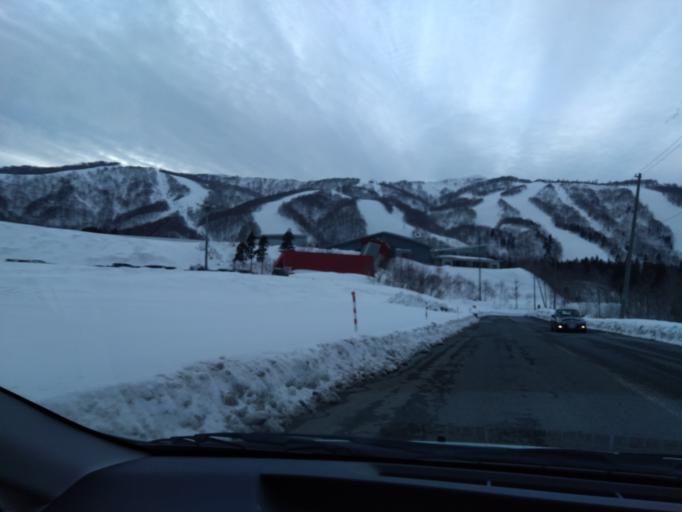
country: JP
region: Iwate
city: Kitakami
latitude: 39.2372
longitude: 140.9089
